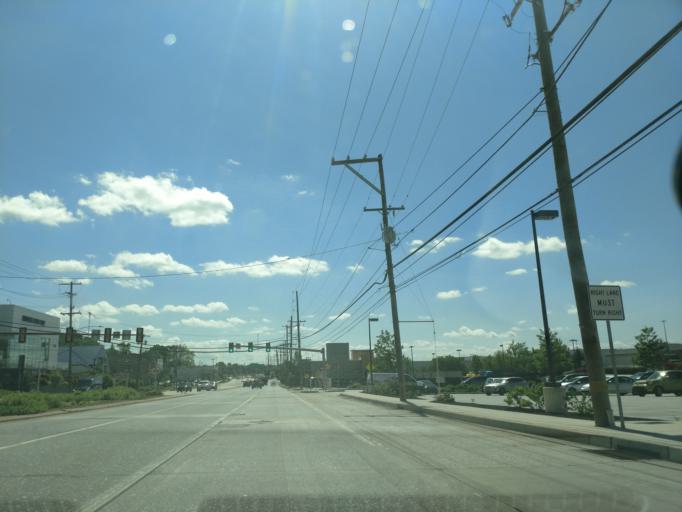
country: US
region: Pennsylvania
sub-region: Montgomery County
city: King of Prussia
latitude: 40.0876
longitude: -75.3838
